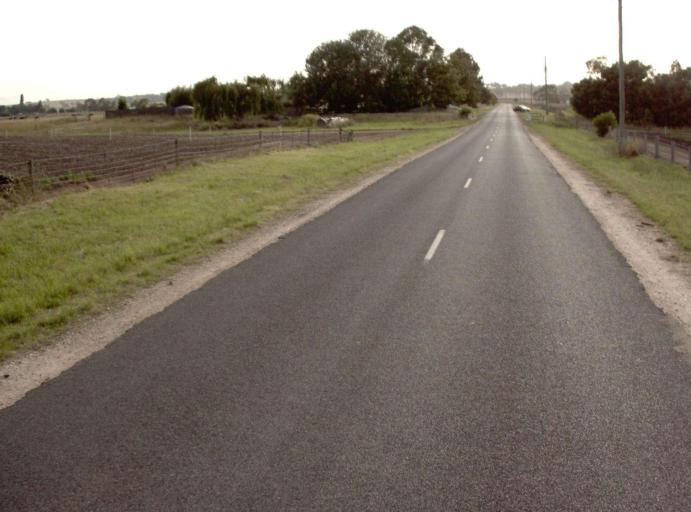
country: AU
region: Victoria
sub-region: Wellington
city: Heyfield
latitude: -37.8768
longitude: 146.9955
